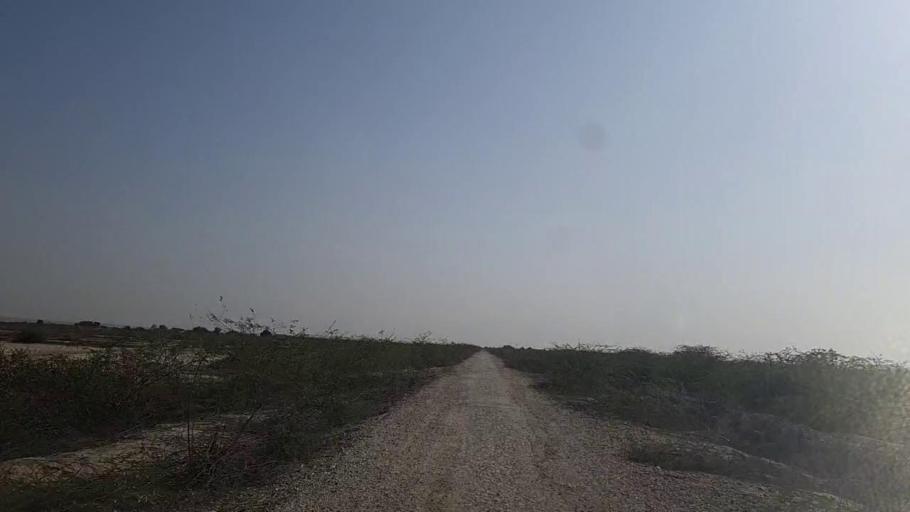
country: PK
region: Sindh
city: Naukot
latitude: 24.5992
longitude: 69.2642
